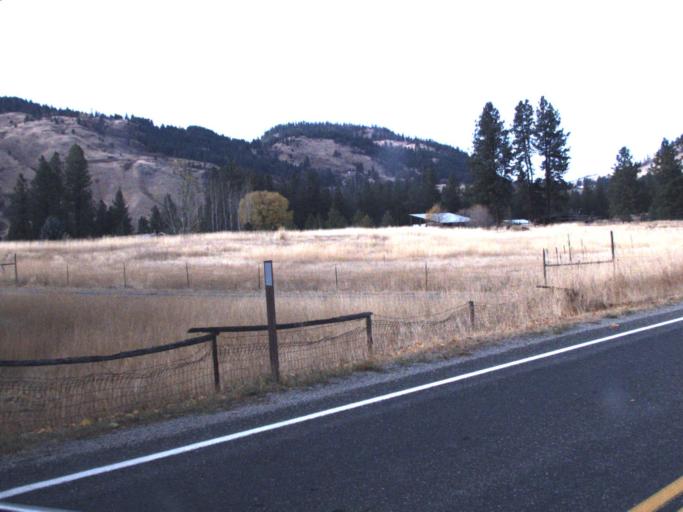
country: US
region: Washington
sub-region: Stevens County
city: Kettle Falls
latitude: 48.7373
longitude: -118.0493
